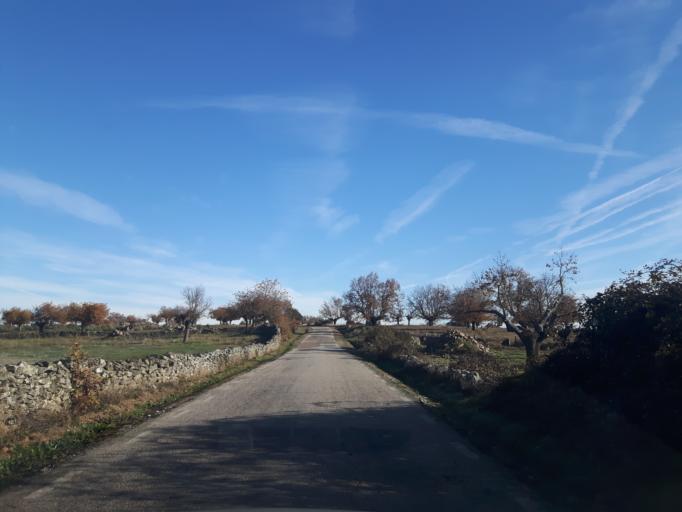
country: ES
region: Castille and Leon
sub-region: Provincia de Salamanca
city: Cerralbo
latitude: 40.9572
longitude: -6.5986
